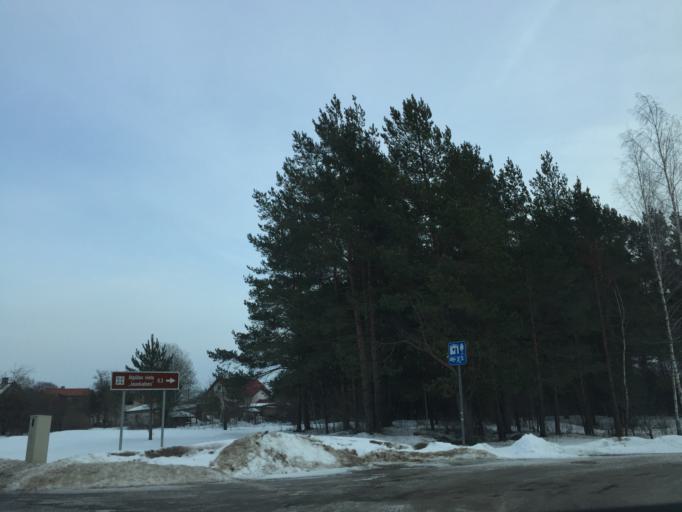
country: LV
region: Salaspils
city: Salaspils
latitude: 56.8440
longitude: 24.4303
